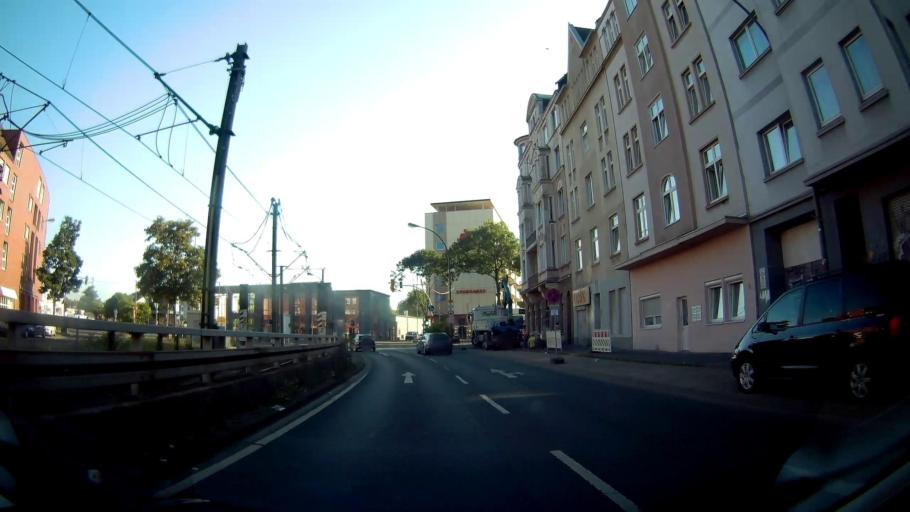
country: DE
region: North Rhine-Westphalia
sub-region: Regierungsbezirk Arnsberg
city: Dortmund
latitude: 51.5280
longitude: 7.4610
